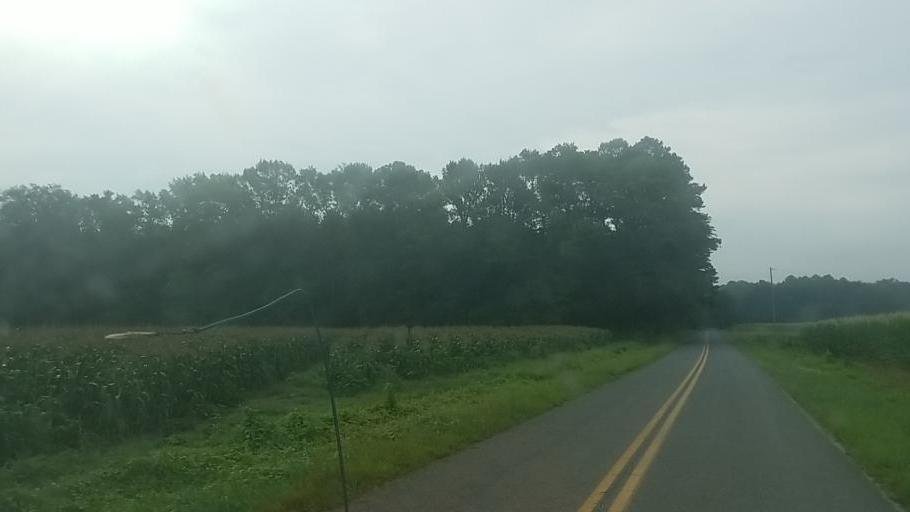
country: US
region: Maryland
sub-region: Wicomico County
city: Pittsville
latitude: 38.4324
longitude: -75.3232
